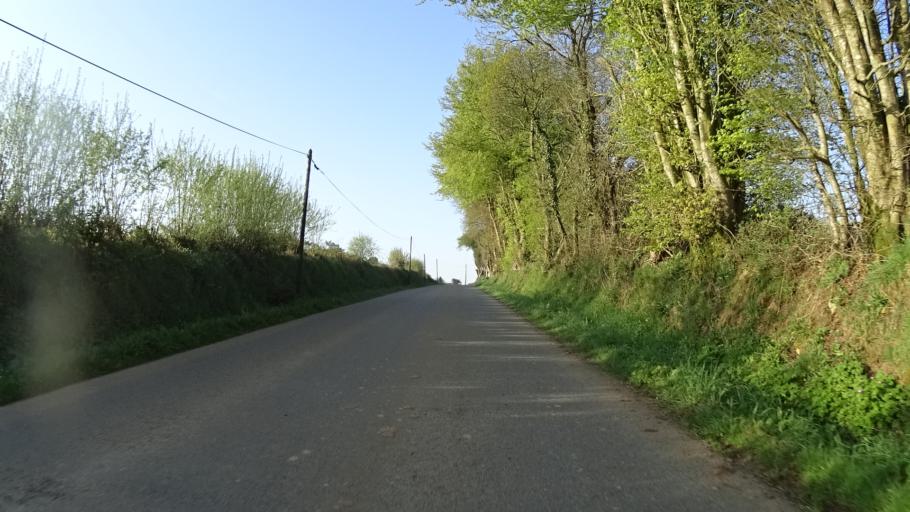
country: FR
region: Brittany
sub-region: Departement du Finistere
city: Sizun
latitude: 48.4304
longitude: -4.0718
